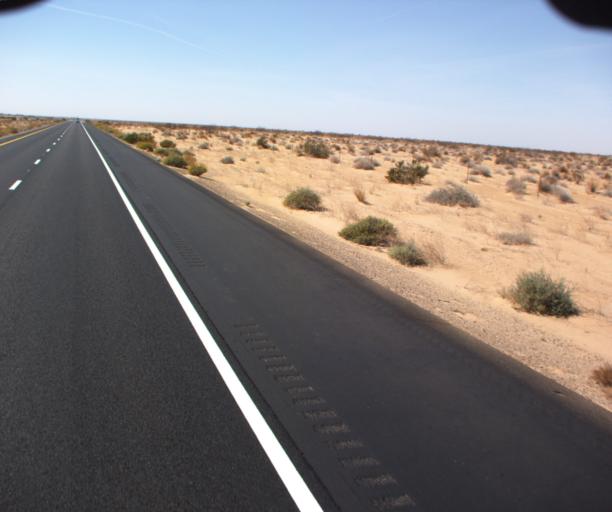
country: US
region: Arizona
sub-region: Yuma County
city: Somerton
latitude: 32.4954
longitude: -114.6036
